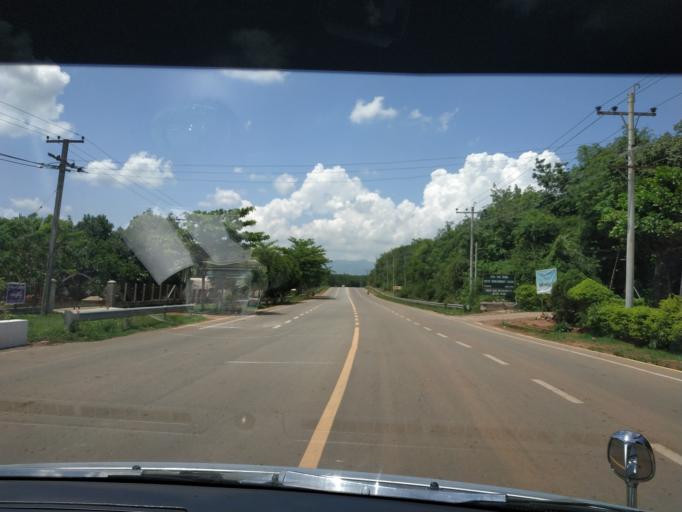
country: MM
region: Mon
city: Kyaikto
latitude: 17.3258
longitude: 97.0242
